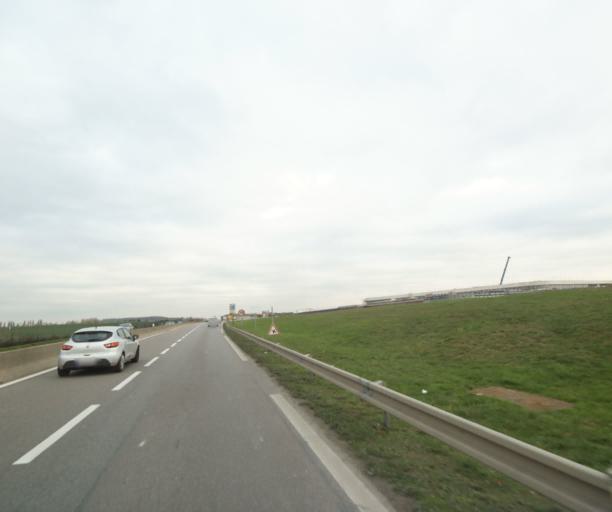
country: FR
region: Ile-de-France
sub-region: Departement du Val-d'Oise
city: Gonesse
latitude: 48.9705
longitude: 2.4579
